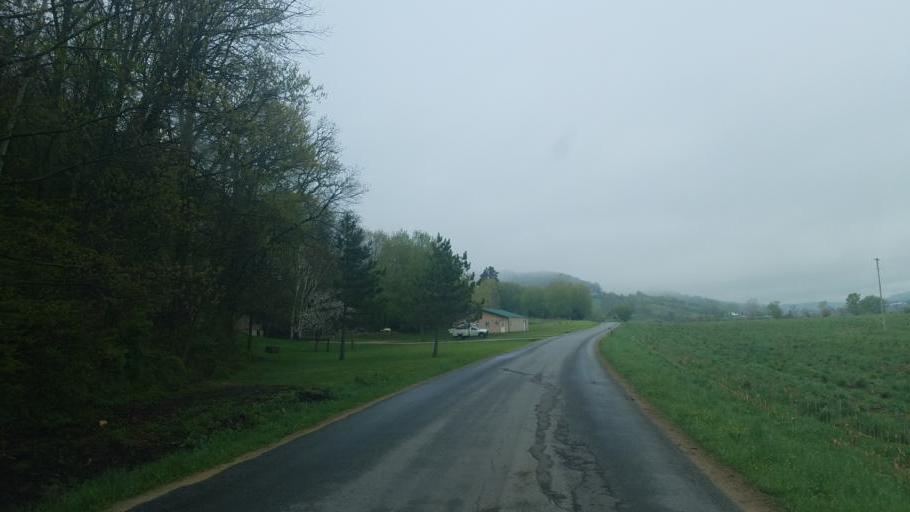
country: US
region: Wisconsin
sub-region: Vernon County
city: Hillsboro
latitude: 43.6239
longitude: -90.3667
